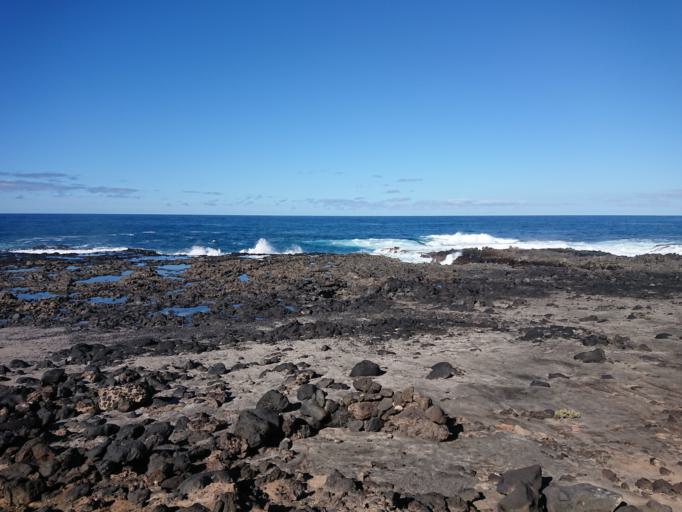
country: ES
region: Canary Islands
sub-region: Provincia de Las Palmas
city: Tinajo
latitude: 29.0831
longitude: -13.7241
